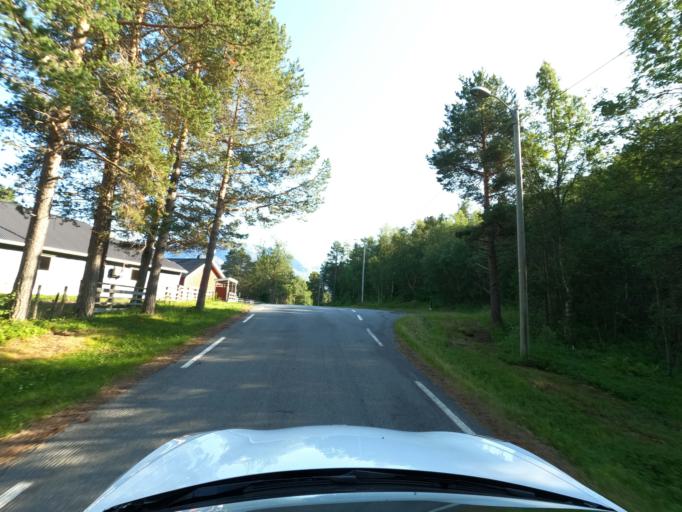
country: NO
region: Nordland
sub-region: Narvik
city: Bjerkvik
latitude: 68.4790
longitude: 17.5279
